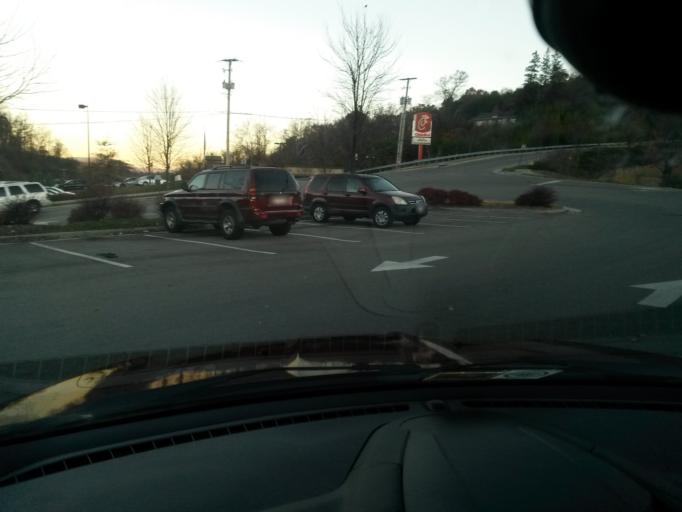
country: US
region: Virginia
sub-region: Roanoke County
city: Narrows
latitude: 37.2256
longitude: -79.9686
